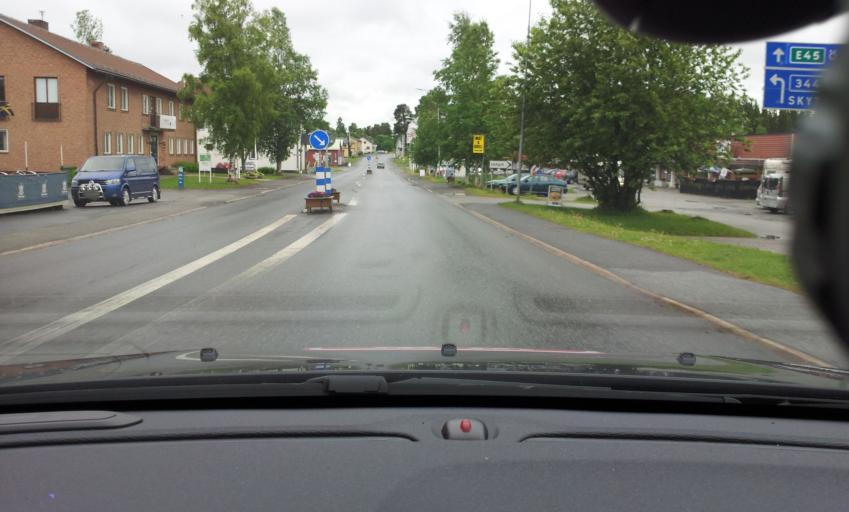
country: SE
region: Jaemtland
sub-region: Stroemsunds Kommun
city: Stroemsund
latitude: 63.5835
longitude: 15.3518
